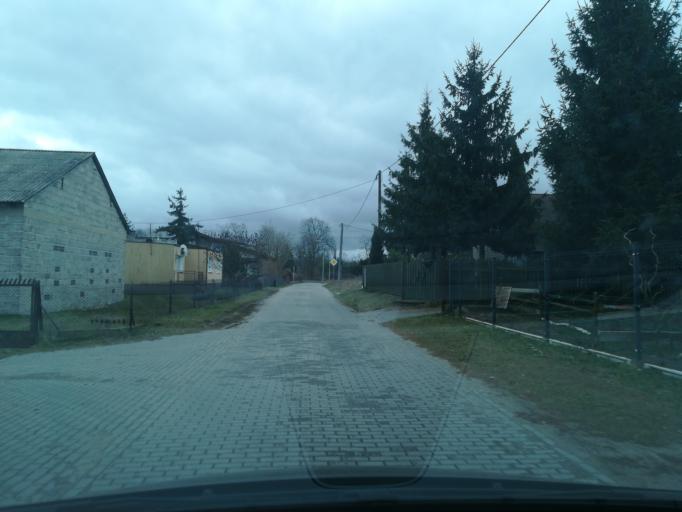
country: PL
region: Kujawsko-Pomorskie
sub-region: Powiat aleksandrowski
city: Ciechocinek
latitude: 52.8749
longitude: 18.7581
